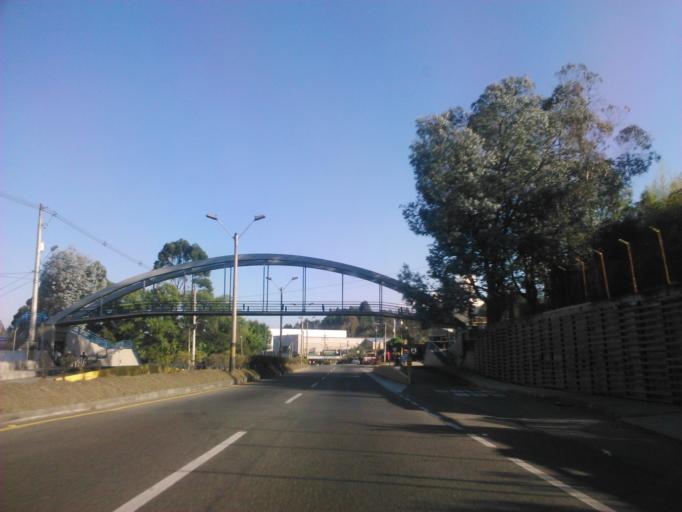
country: CO
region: Antioquia
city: Guarne
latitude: 6.2987
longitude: -75.4549
